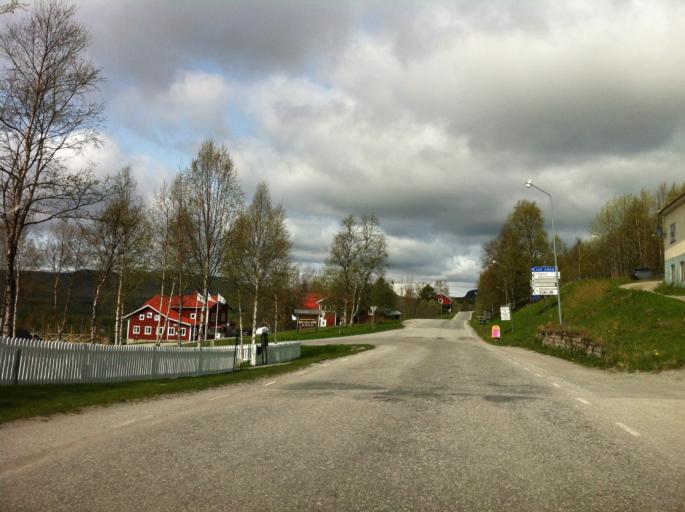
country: NO
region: Hedmark
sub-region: Engerdal
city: Engerdal
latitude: 62.4388
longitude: 12.7003
